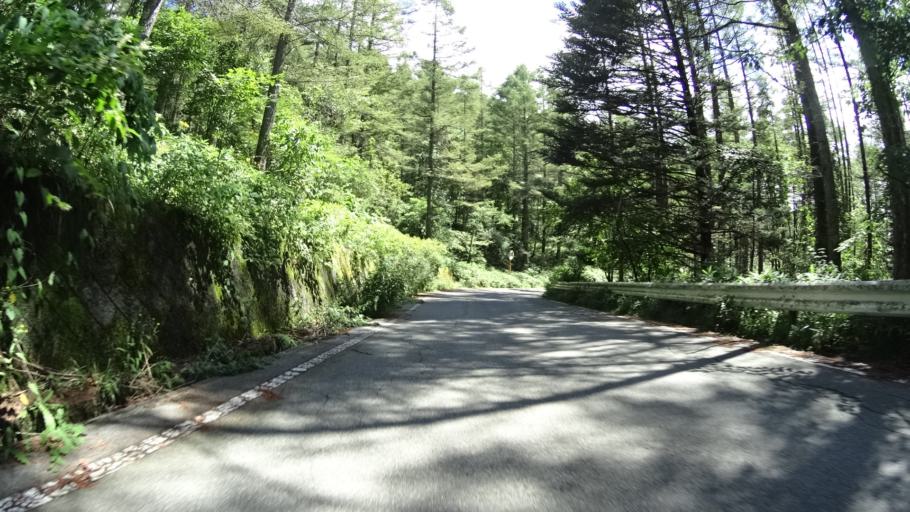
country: JP
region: Yamanashi
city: Enzan
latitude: 35.7305
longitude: 138.8428
